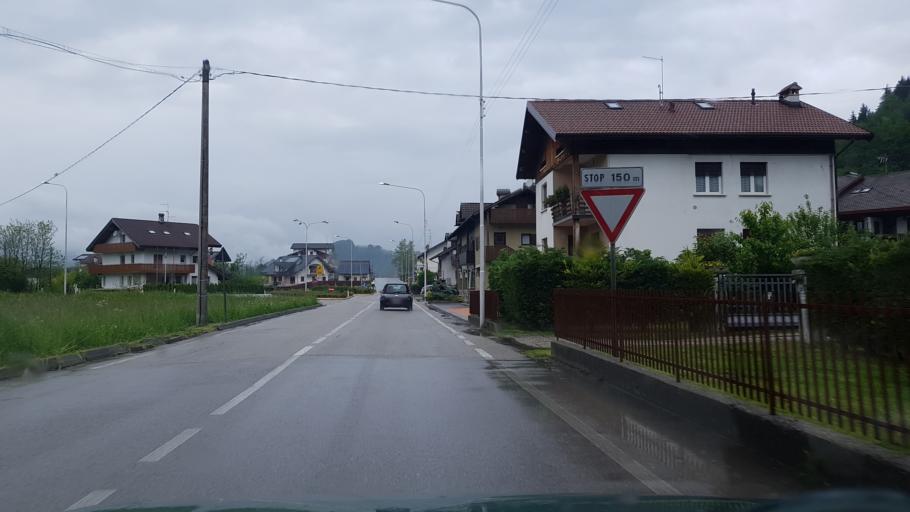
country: IT
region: Veneto
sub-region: Provincia di Belluno
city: Farra d'Alpago
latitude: 46.1225
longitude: 12.3569
